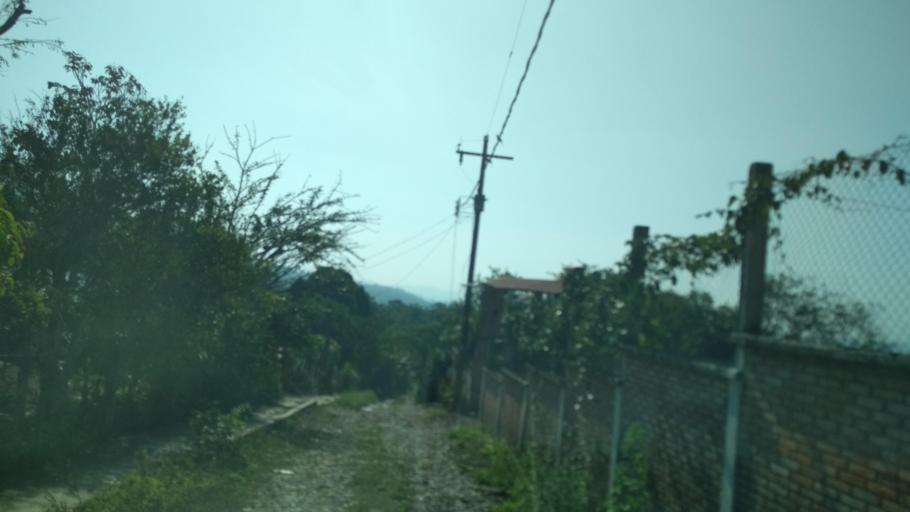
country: MX
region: Veracruz
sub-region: Papantla
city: Polutla
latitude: 20.4641
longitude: -97.1949
